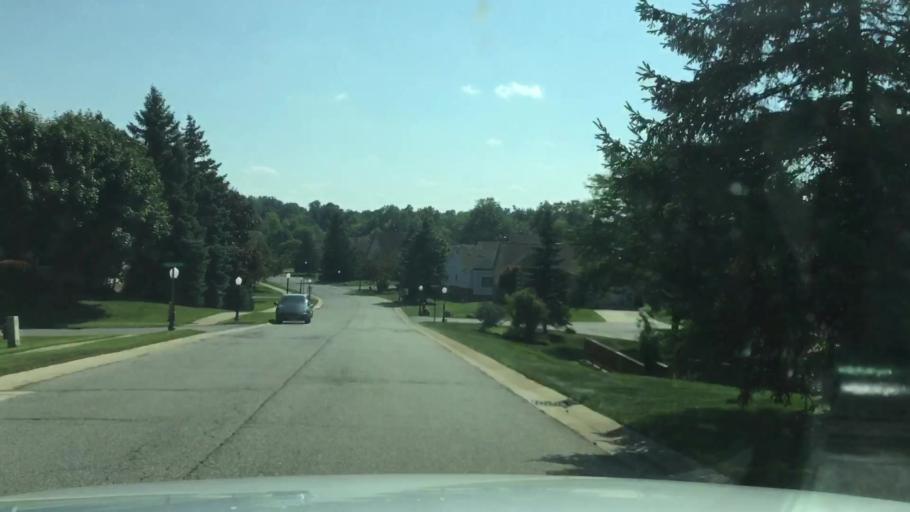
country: US
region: Michigan
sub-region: Oakland County
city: Walled Lake
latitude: 42.5237
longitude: -83.4566
